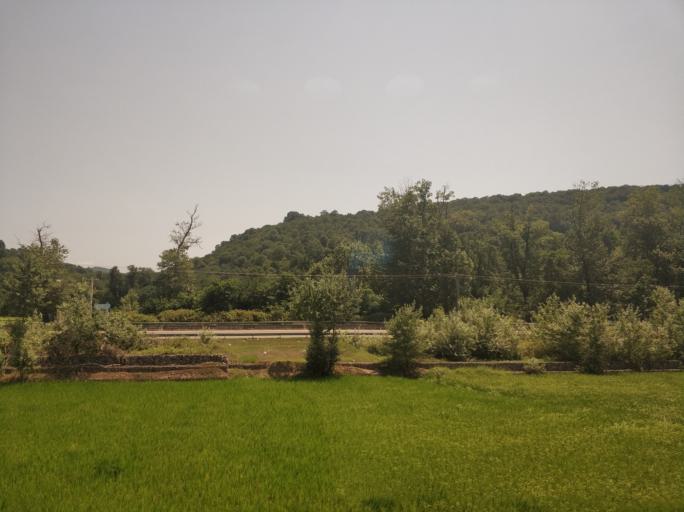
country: IR
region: Gilan
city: Pa'in-e Bazar-e Rudbar
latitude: 36.9599
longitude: 49.5536
